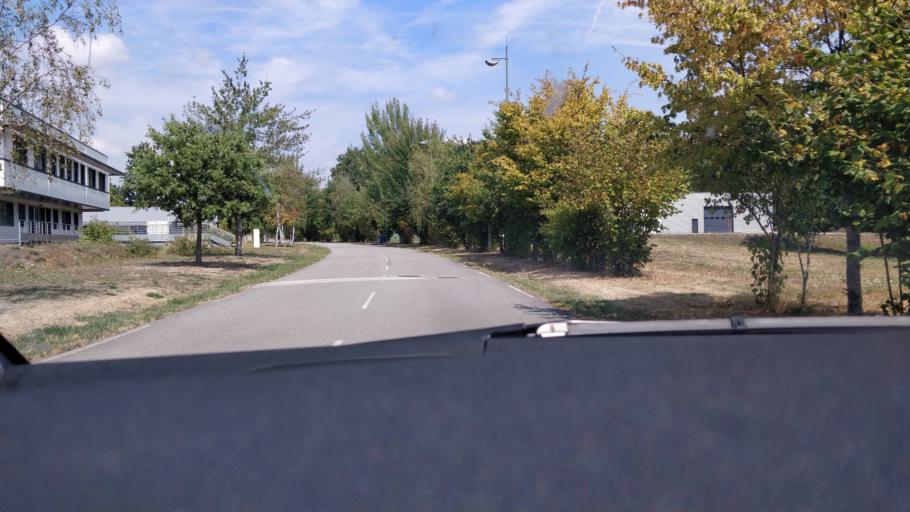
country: FR
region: Limousin
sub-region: Departement de la Haute-Vienne
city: Le Palais-sur-Vienne
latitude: 45.8574
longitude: 1.2990
